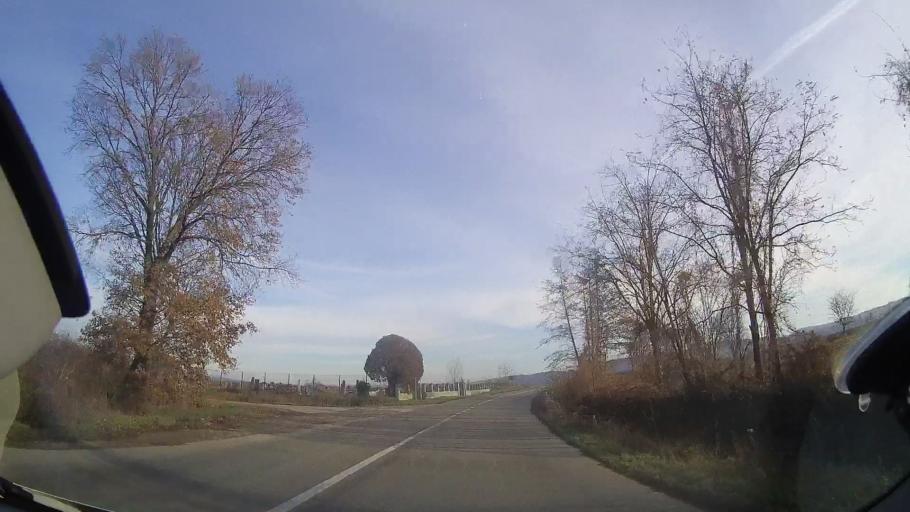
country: RO
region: Bihor
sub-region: Comuna Tetchea
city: Hotar
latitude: 47.0540
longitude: 22.2807
